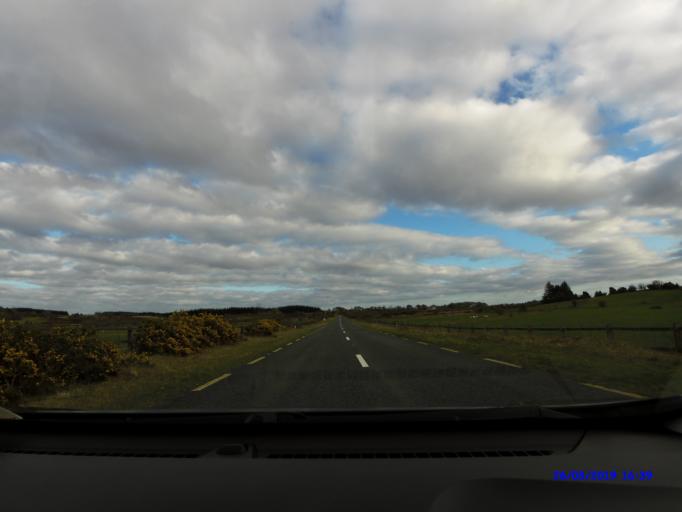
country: IE
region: Connaught
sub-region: Maigh Eo
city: Ballyhaunis
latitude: 53.8830
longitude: -8.7925
